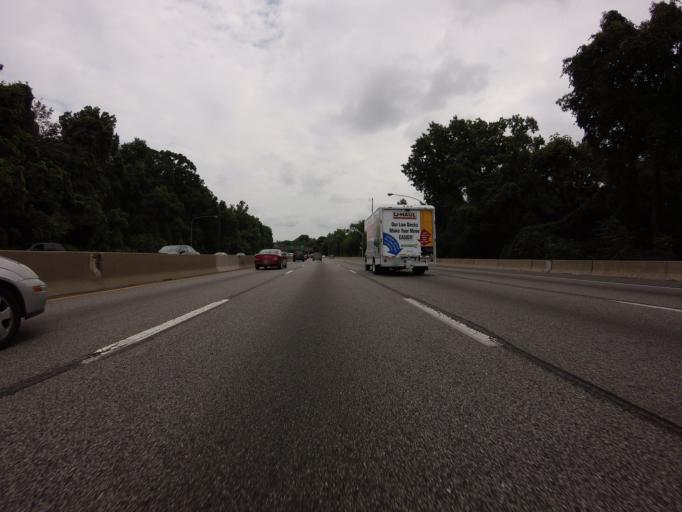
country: US
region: Pennsylvania
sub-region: Montgomery County
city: Bala-Cynwyd
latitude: 39.9944
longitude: -75.1987
